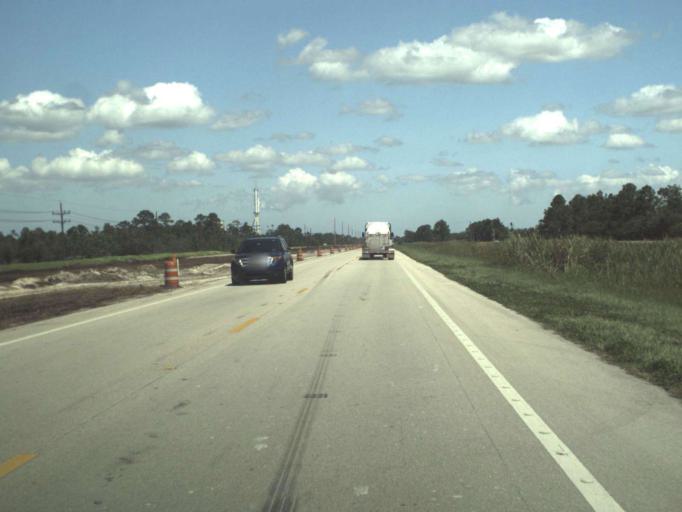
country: US
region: Florida
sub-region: Palm Beach County
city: Limestone Creek
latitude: 26.9245
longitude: -80.3241
